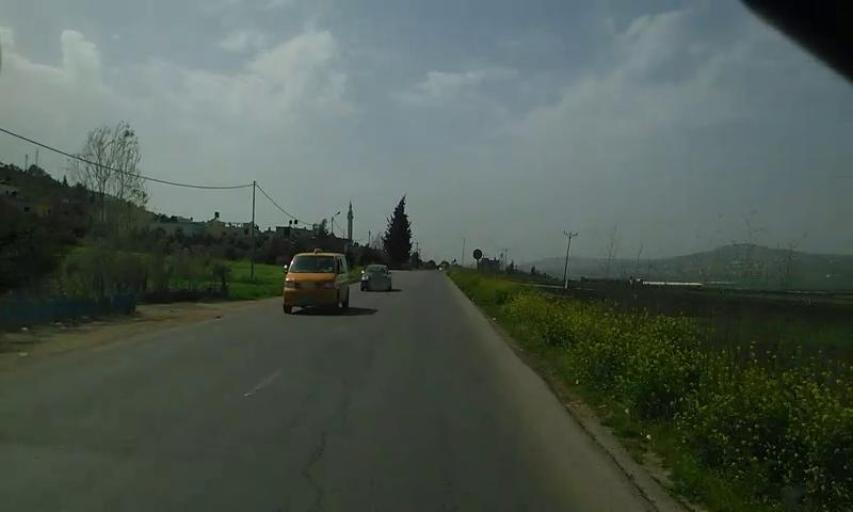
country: PS
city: Bir al Basha
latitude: 32.4251
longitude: 35.2426
